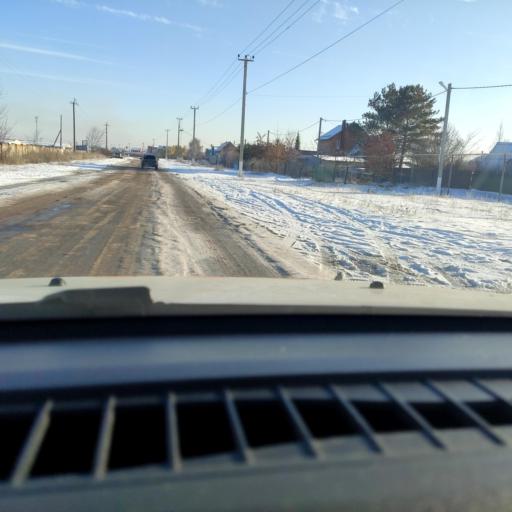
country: RU
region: Samara
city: Podstepki
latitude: 53.5195
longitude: 49.1377
